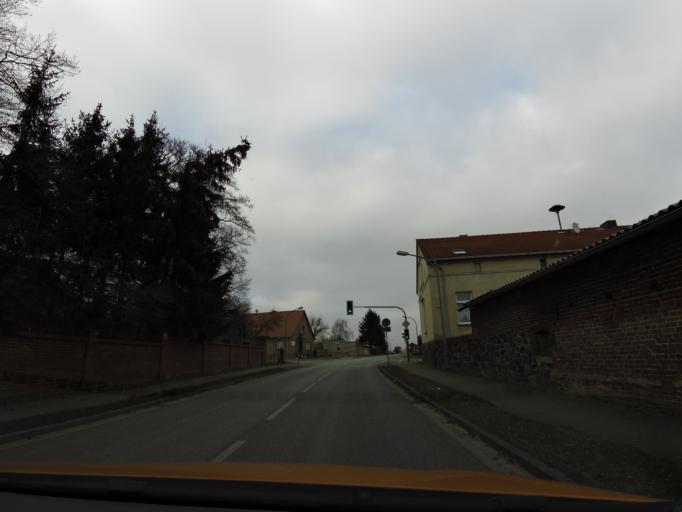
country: DE
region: Brandenburg
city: Walsleben
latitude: 52.8863
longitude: 12.6421
